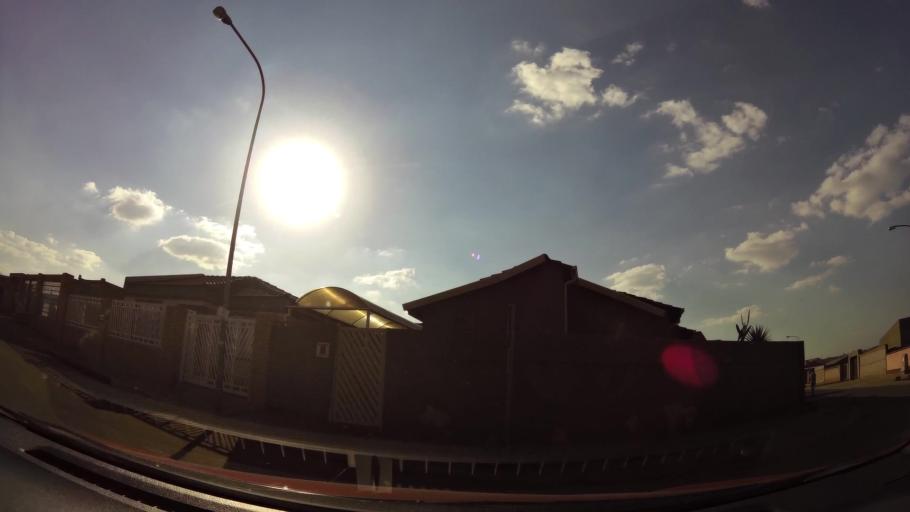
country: ZA
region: Gauteng
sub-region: City of Johannesburg Metropolitan Municipality
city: Soweto
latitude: -26.2169
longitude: 27.8745
